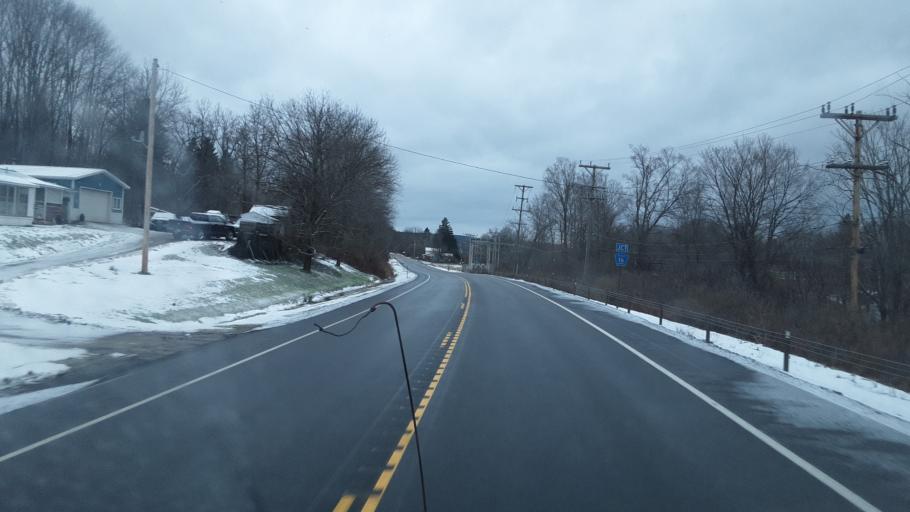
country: US
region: New York
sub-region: Allegany County
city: Belmont
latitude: 42.2937
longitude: -78.0726
